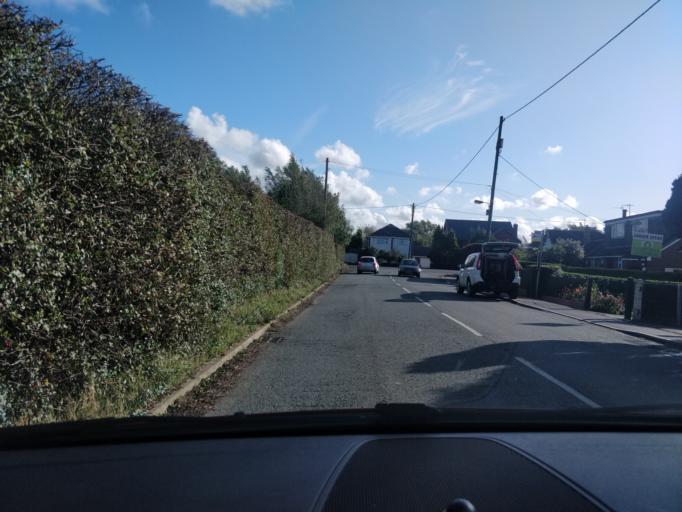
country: GB
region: England
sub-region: Lancashire
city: Banks
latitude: 53.6838
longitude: -2.9128
